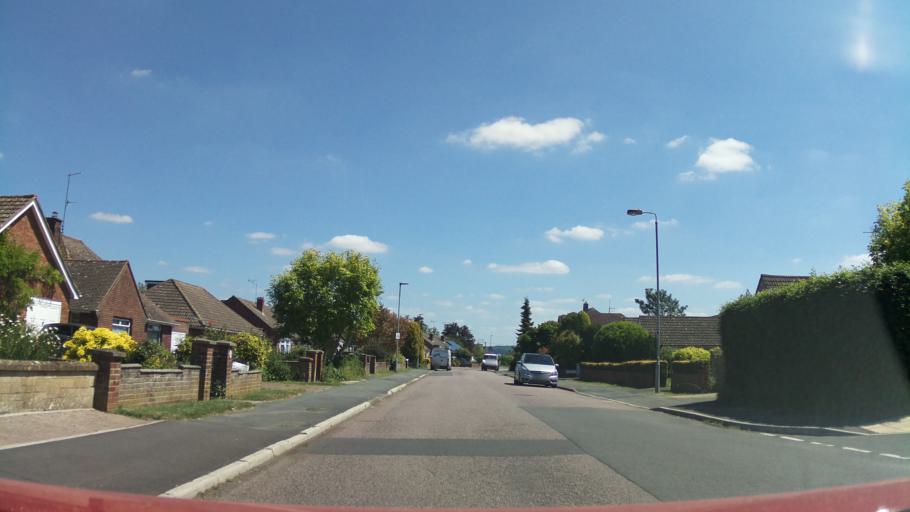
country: GB
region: England
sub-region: Wiltshire
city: Royal Wootton Bassett
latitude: 51.5463
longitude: -1.8958
